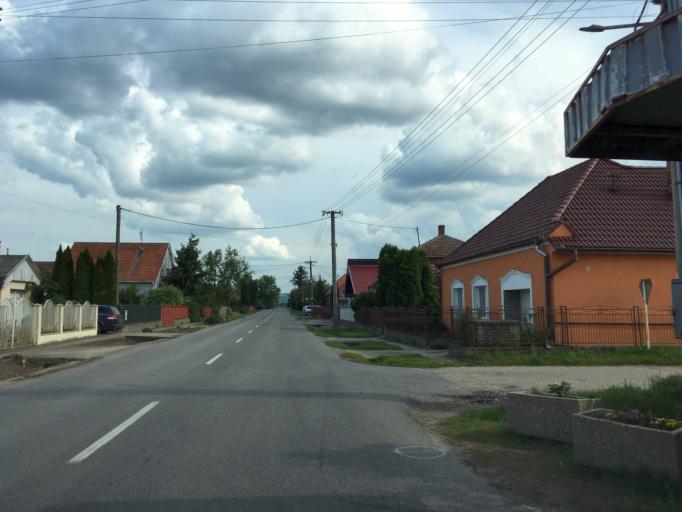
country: HU
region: Komarom-Esztergom
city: Dunaalmas
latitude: 47.7781
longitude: 18.2978
